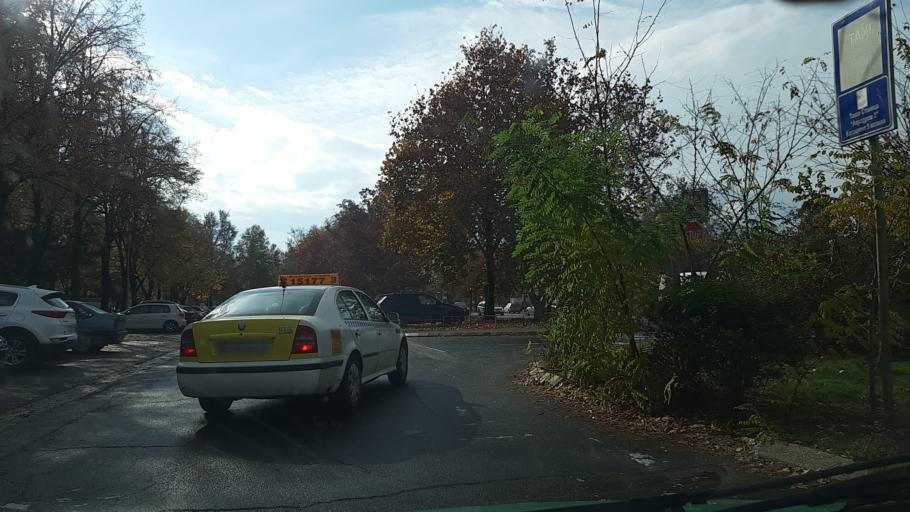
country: MK
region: Kisela Voda
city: Usje
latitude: 41.9891
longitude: 21.4635
